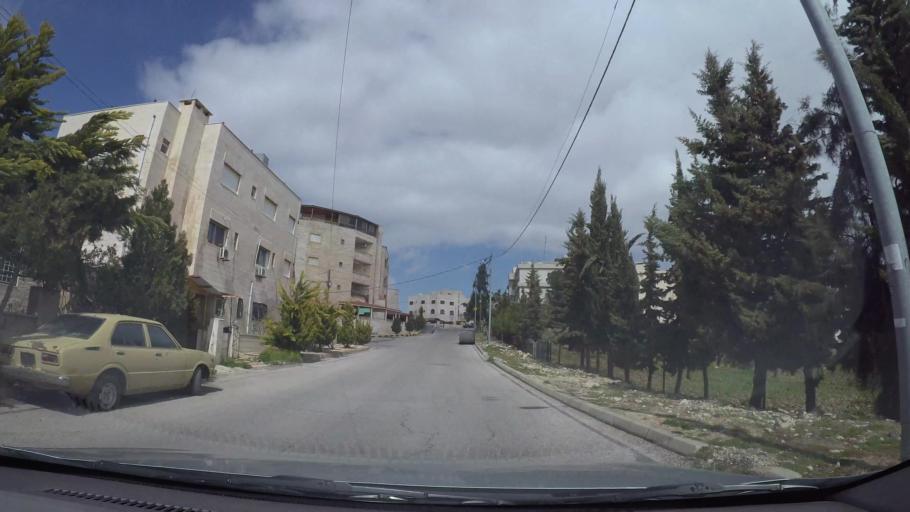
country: JO
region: Amman
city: Al Jubayhah
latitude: 31.9932
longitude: 35.8525
